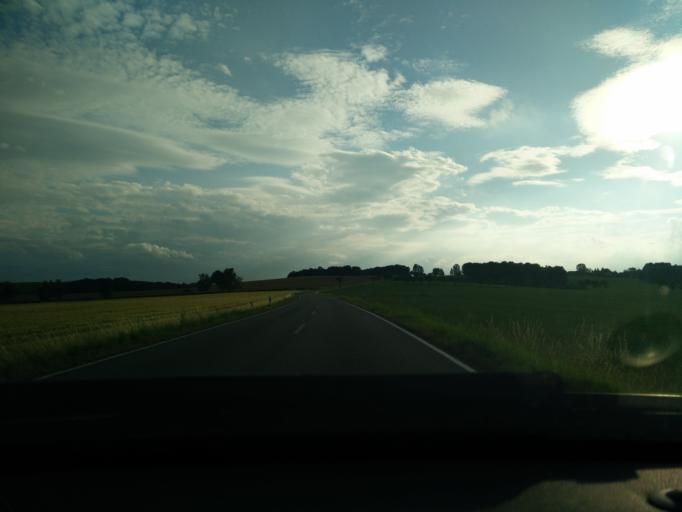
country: DE
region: Saxony
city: Konigsfeld
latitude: 51.0584
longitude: 12.7448
